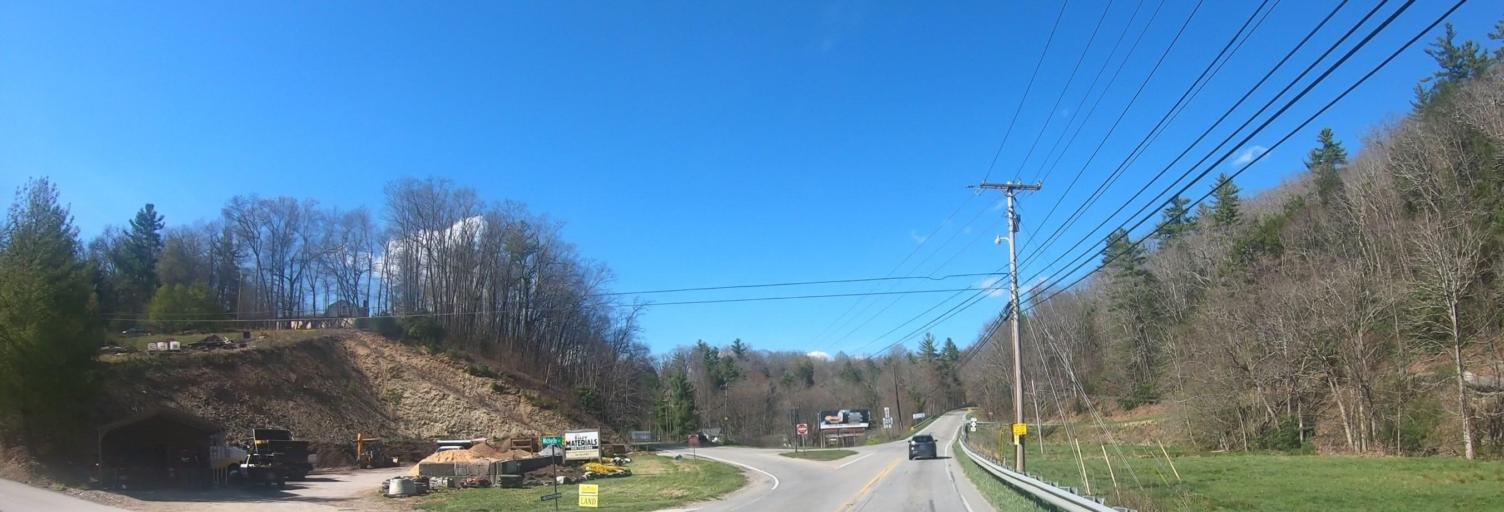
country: US
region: North Carolina
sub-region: Avery County
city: Newland
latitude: 36.0315
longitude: -81.9136
